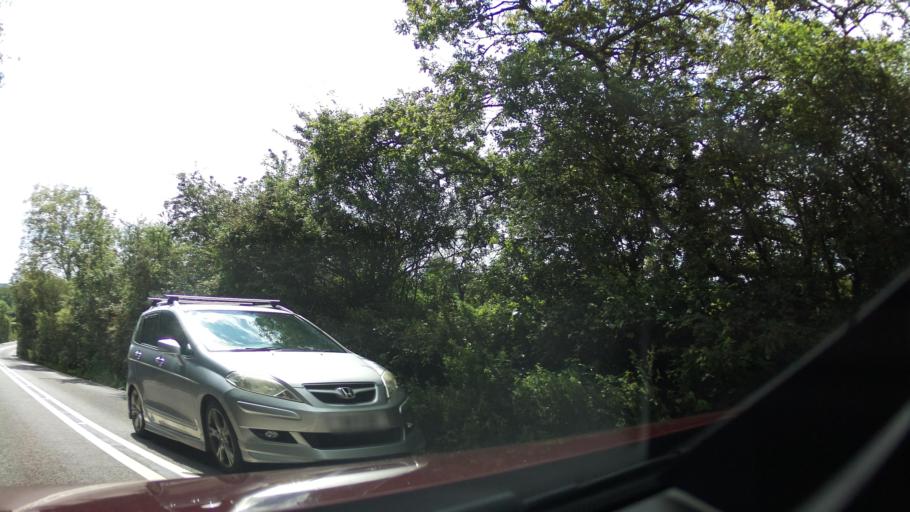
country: GB
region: England
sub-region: Devon
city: Teignmouth
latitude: 50.5161
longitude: -3.5173
